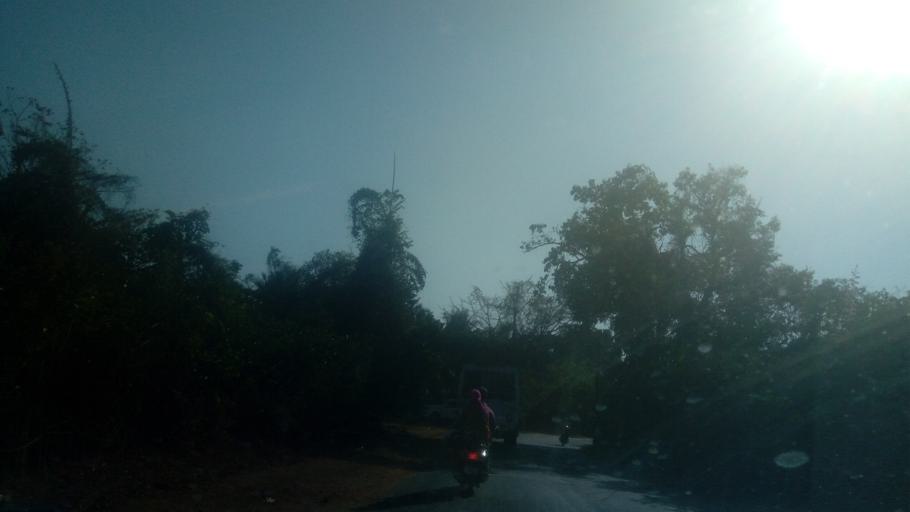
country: IN
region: Goa
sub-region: North Goa
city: Jua
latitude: 15.5245
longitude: 73.9658
